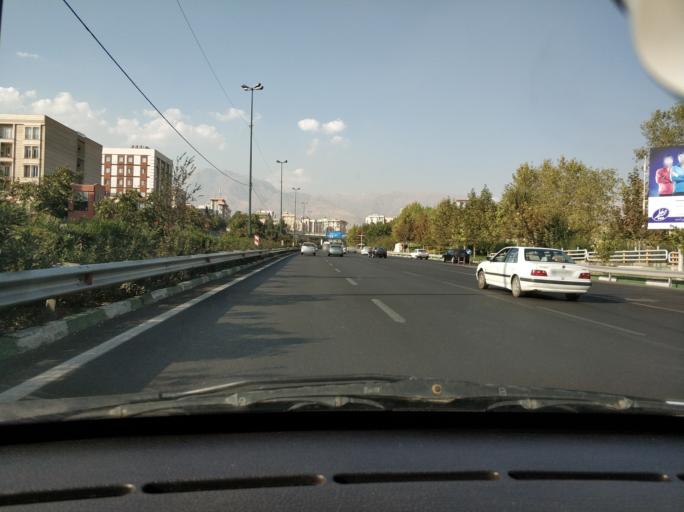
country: IR
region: Tehran
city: Tajrish
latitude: 35.7579
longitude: 51.4655
